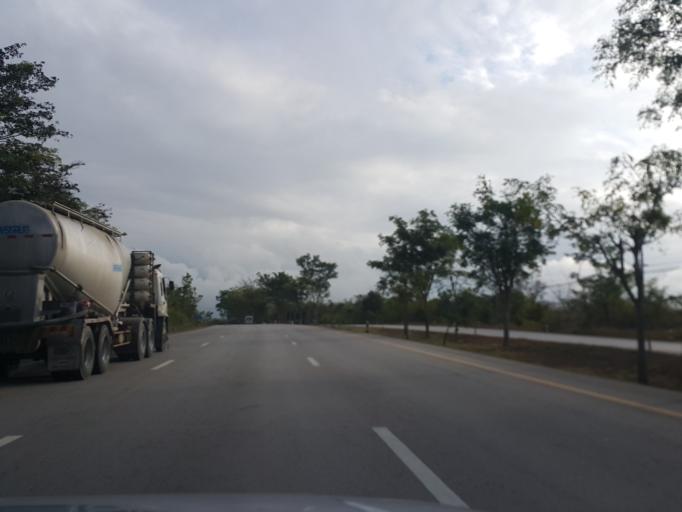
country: TH
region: Lampang
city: Ko Kha
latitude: 18.1328
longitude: 99.3907
